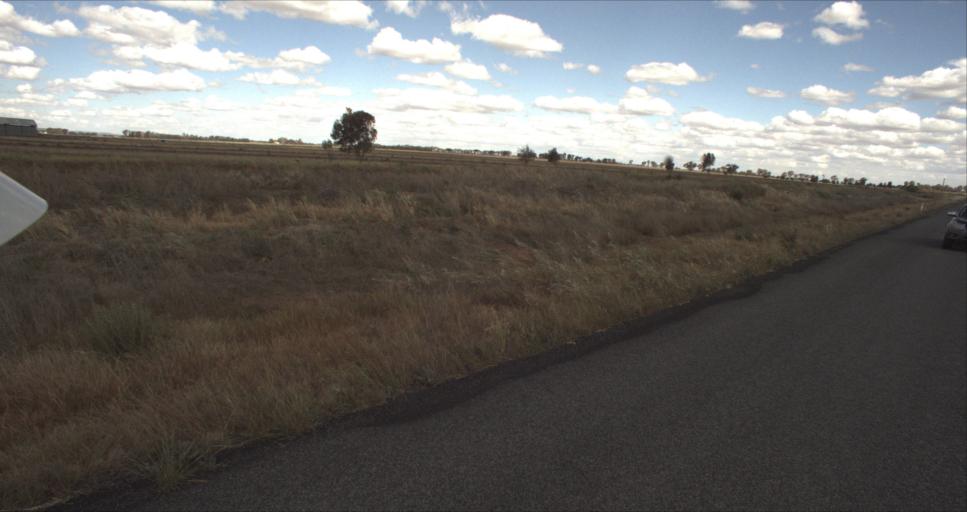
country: AU
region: New South Wales
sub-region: Leeton
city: Leeton
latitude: -34.4474
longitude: 146.2552
